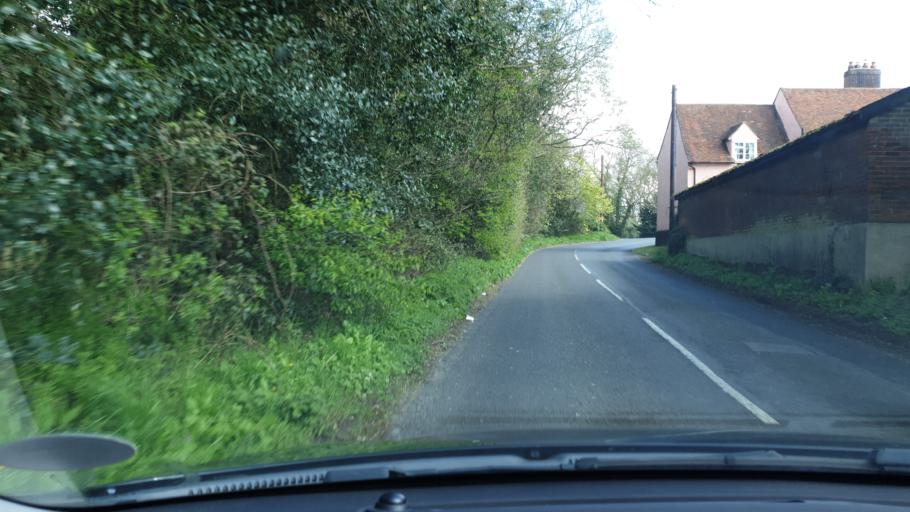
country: GB
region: England
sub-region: Essex
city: Great Bentley
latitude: 51.8750
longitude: 1.1111
